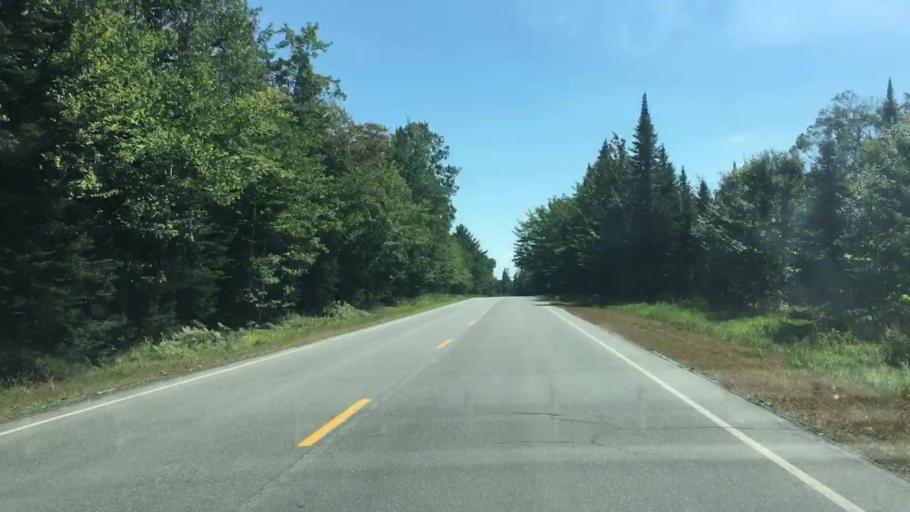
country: US
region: Maine
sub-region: Piscataquis County
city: Milo
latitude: 45.2044
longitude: -68.9081
